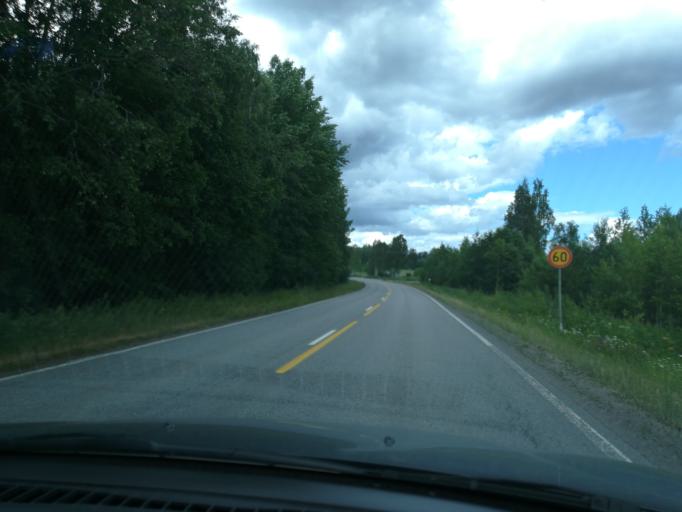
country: FI
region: Southern Savonia
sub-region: Mikkeli
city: Hirvensalmi
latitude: 61.6691
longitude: 26.7638
